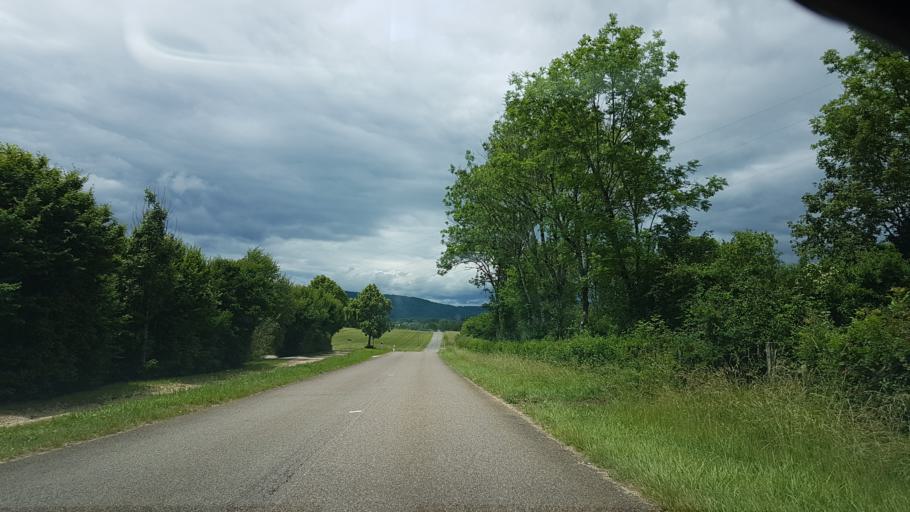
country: FR
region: Franche-Comte
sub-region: Departement du Jura
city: Clairvaux-les-Lacs
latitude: 46.5807
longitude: 5.7297
